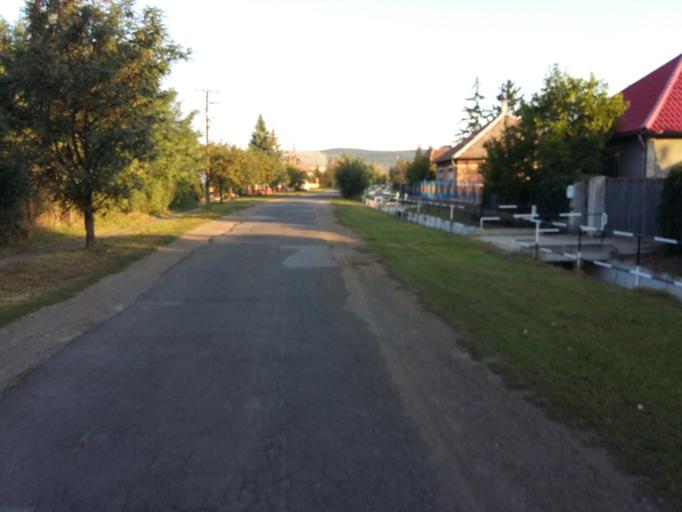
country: HU
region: Borsod-Abauj-Zemplen
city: Bekecs
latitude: 48.1594
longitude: 21.1827
